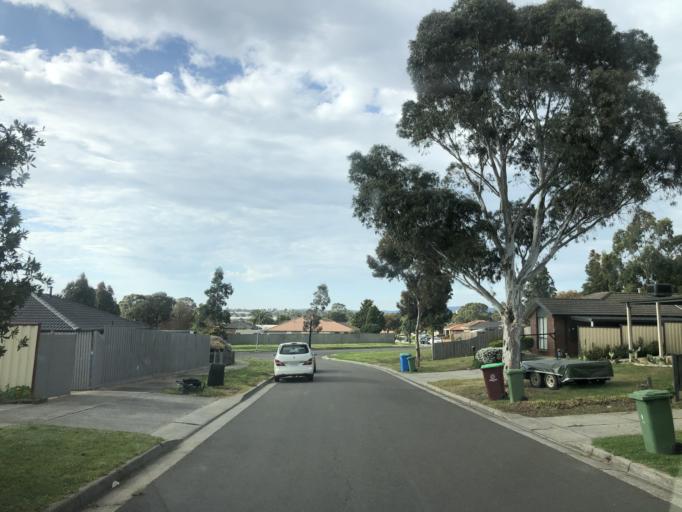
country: AU
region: Victoria
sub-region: Casey
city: Hampton Park
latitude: -38.0229
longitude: 145.2535
